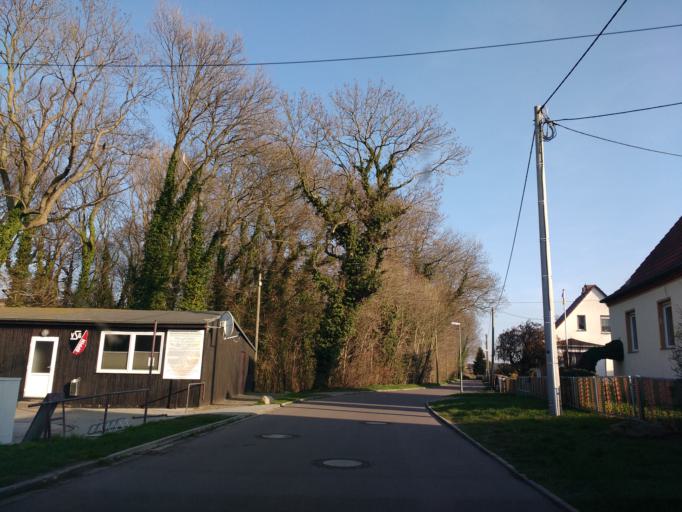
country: DE
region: Saxony-Anhalt
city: Oppin
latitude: 51.5505
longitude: 12.0297
